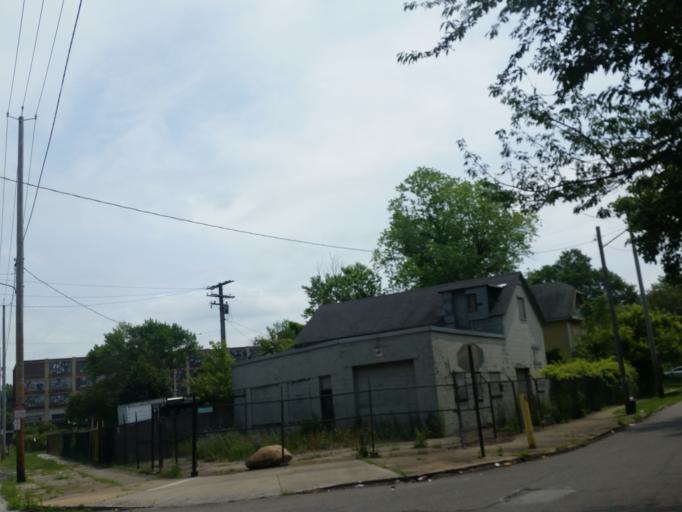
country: US
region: Ohio
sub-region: Cuyahoga County
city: East Cleveland
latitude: 41.5477
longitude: -81.5963
